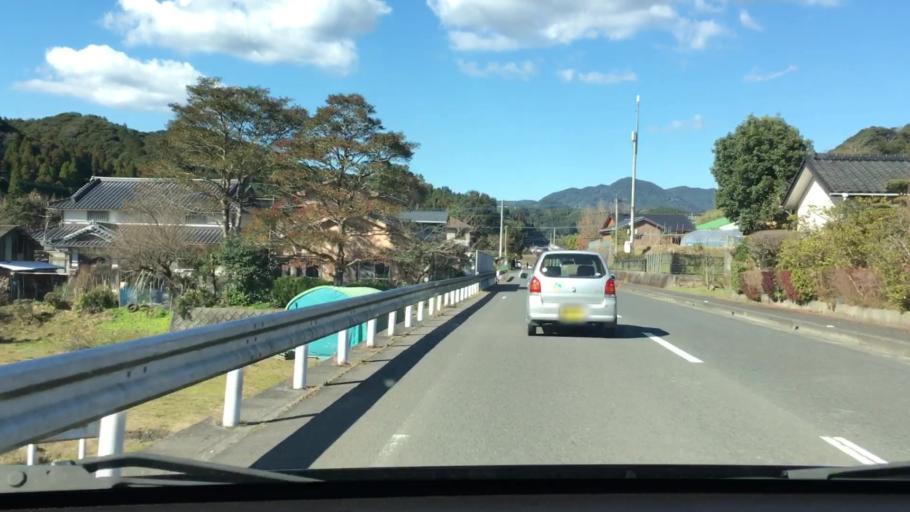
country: JP
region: Kagoshima
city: Ijuin
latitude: 31.6908
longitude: 130.4649
